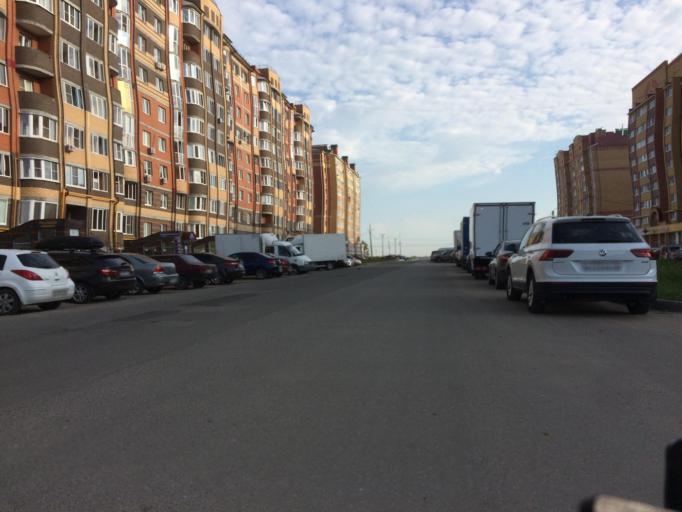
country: RU
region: Mariy-El
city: Medvedevo
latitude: 56.6370
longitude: 47.8123
